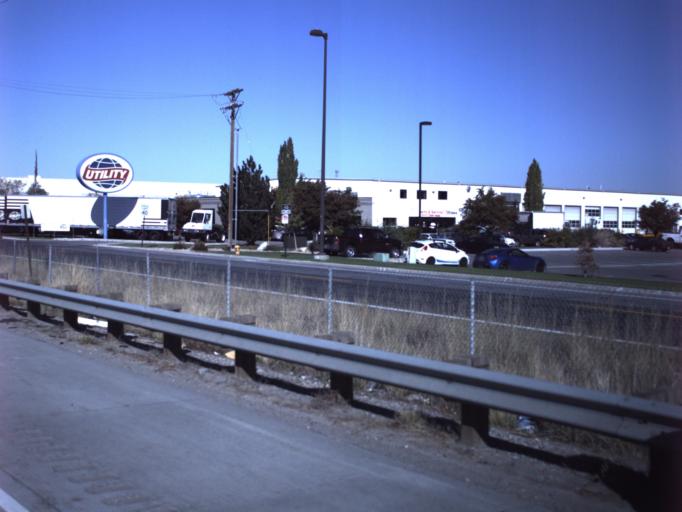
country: US
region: Utah
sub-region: Salt Lake County
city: West Valley City
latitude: 40.7260
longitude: -112.0086
